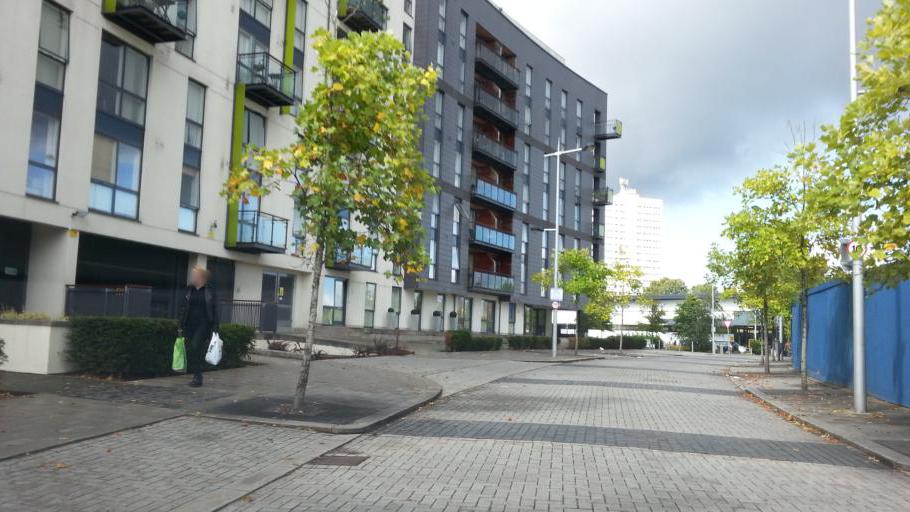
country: GB
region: England
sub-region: City and Borough of Birmingham
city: Birmingham
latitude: 52.4538
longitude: -1.9044
